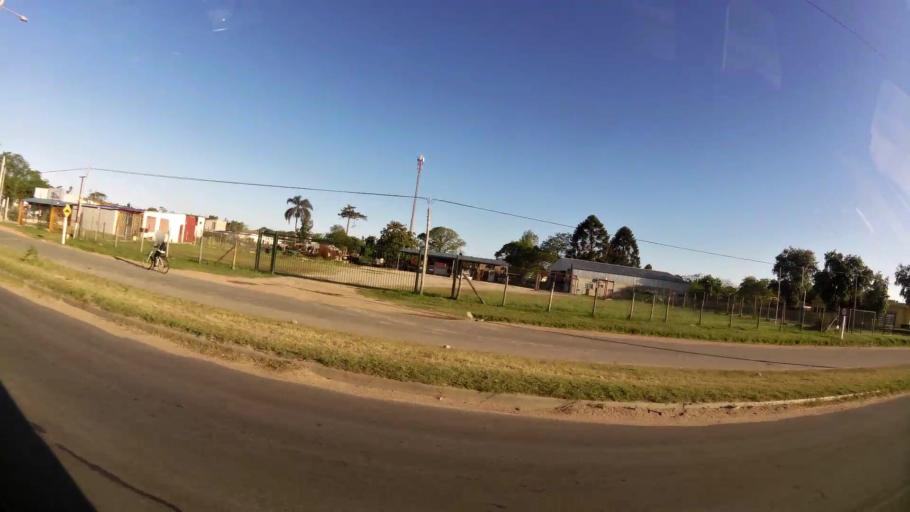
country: UY
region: Canelones
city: Paso de Carrasco
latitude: -34.8625
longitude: -56.0547
